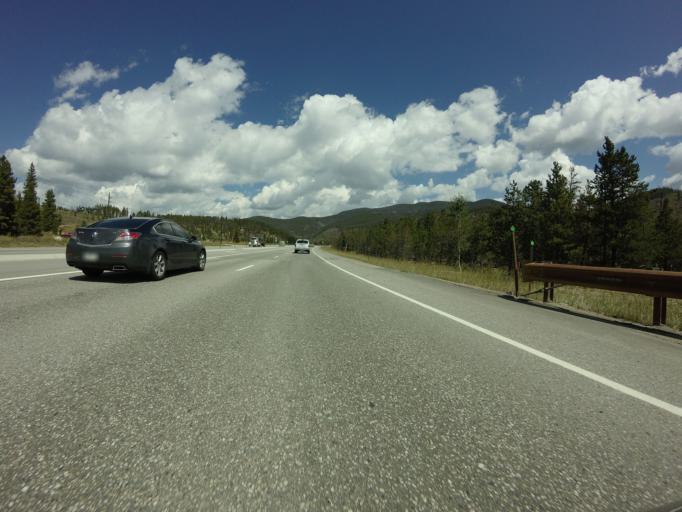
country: US
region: Colorado
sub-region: Summit County
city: Breckenridge
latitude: 39.5406
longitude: -106.0417
